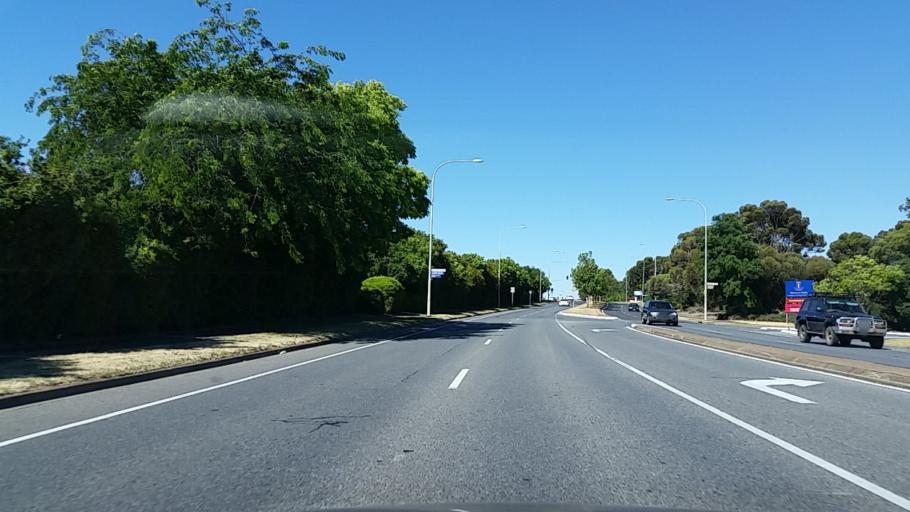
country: AU
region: South Australia
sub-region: Tea Tree Gully
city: Modbury
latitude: -34.7948
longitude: 138.6895
